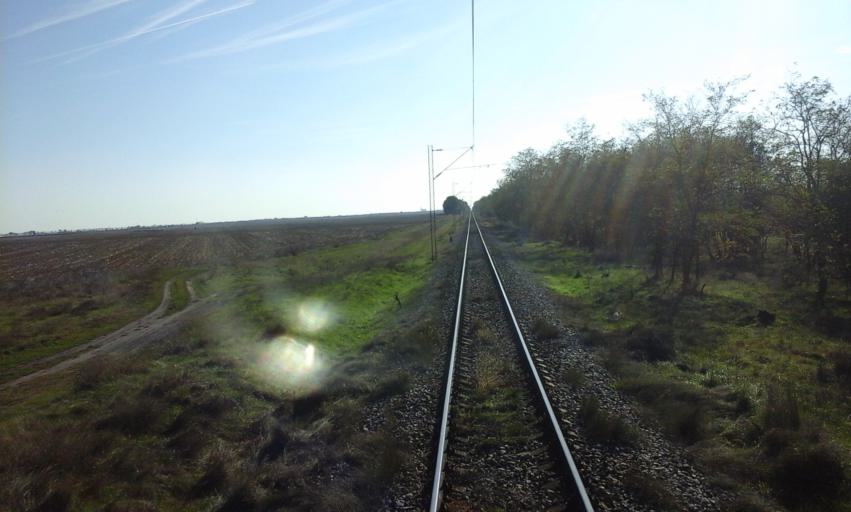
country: RS
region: Autonomna Pokrajina Vojvodina
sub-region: Severnobacki Okrug
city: Backa Topola
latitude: 45.8761
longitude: 19.6585
